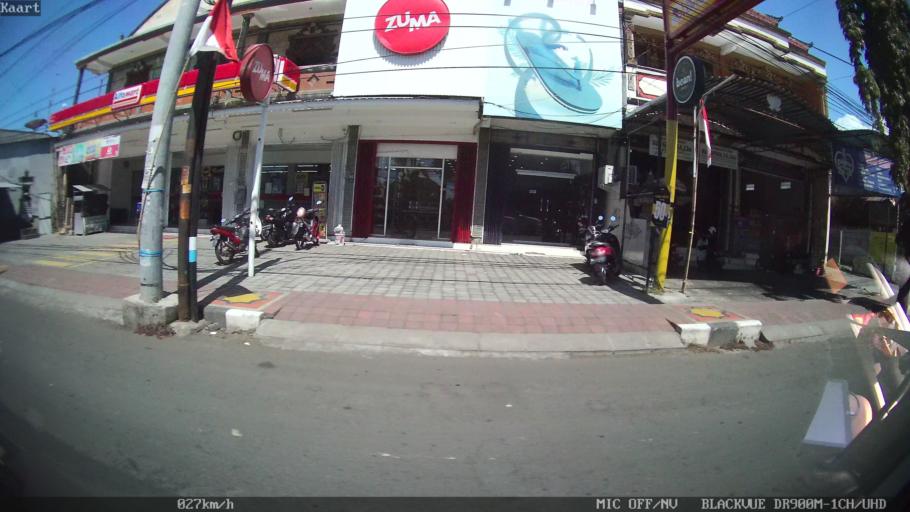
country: ID
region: Bali
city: Banjar Galiran
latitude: -8.1202
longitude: 115.0731
